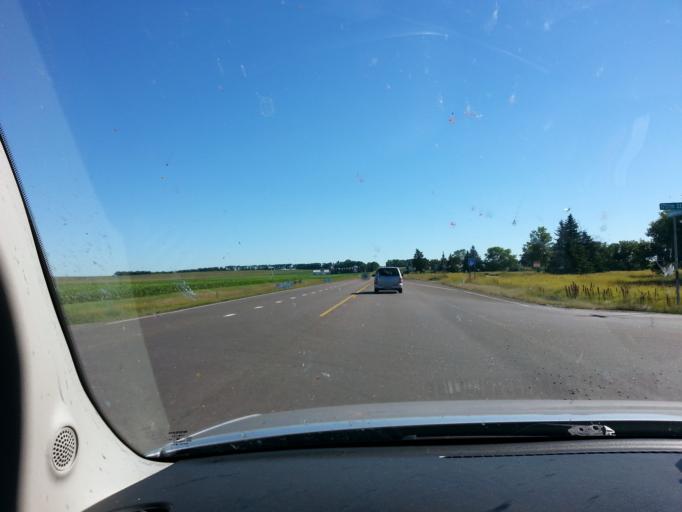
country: US
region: Minnesota
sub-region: Dakota County
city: Rosemount
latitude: 44.7031
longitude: -93.1366
